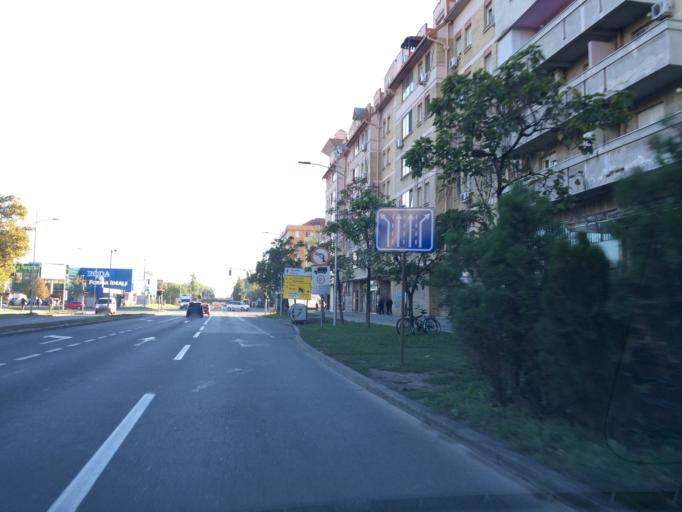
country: RS
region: Autonomna Pokrajina Vojvodina
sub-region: Juznobacki Okrug
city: Novi Sad
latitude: 45.2633
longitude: 19.8159
